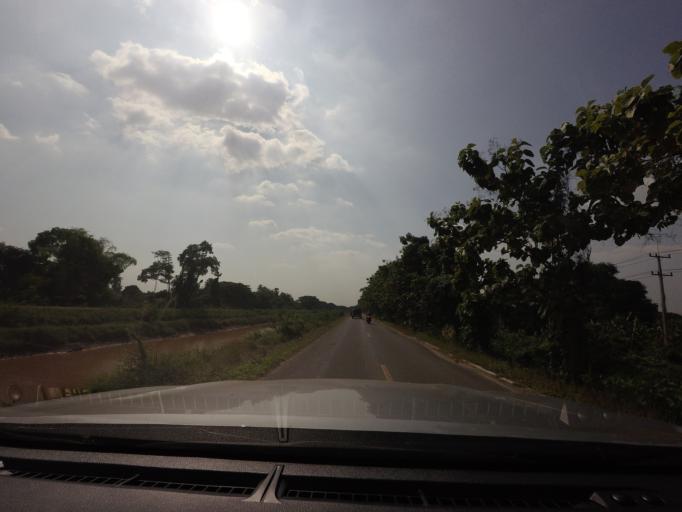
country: TH
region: Phitsanulok
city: Phitsanulok
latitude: 16.8083
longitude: 100.2193
